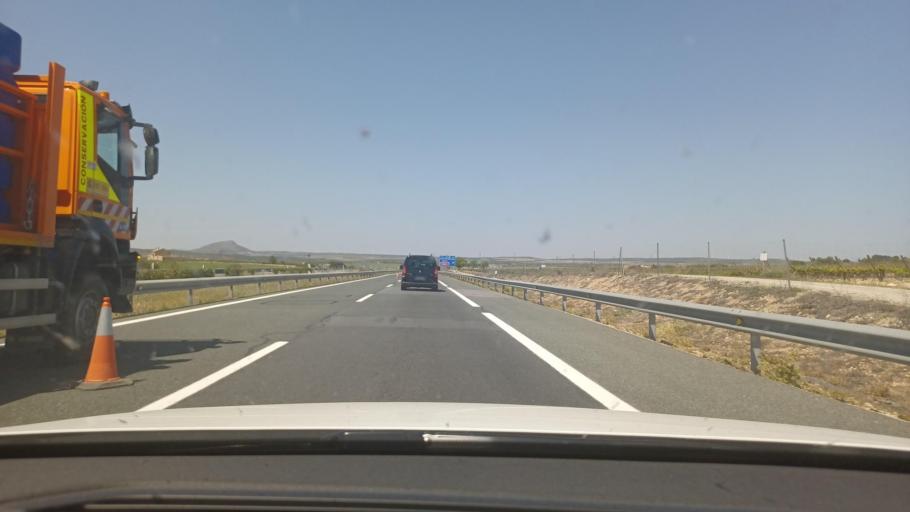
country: ES
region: Castille-La Mancha
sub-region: Provincia de Albacete
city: Alpera
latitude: 38.8795
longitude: -1.2101
